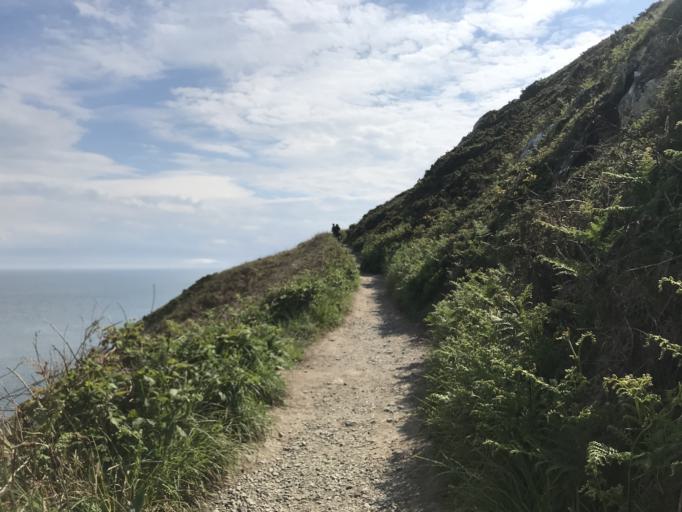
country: IE
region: Leinster
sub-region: Fingal County
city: Howth
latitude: 53.3763
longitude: -6.0463
